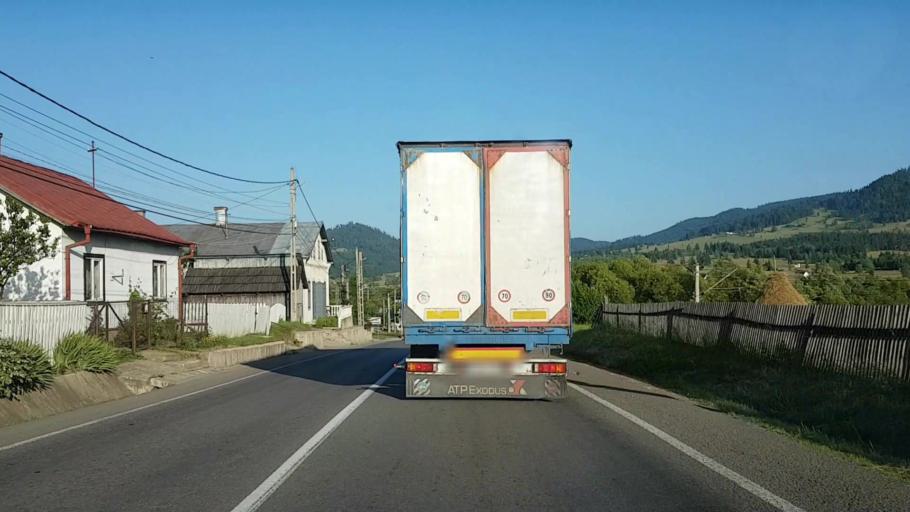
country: RO
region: Suceava
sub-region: Comuna Dorna Candrenilor
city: Dorna Candrenilor
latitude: 47.3581
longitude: 25.2343
